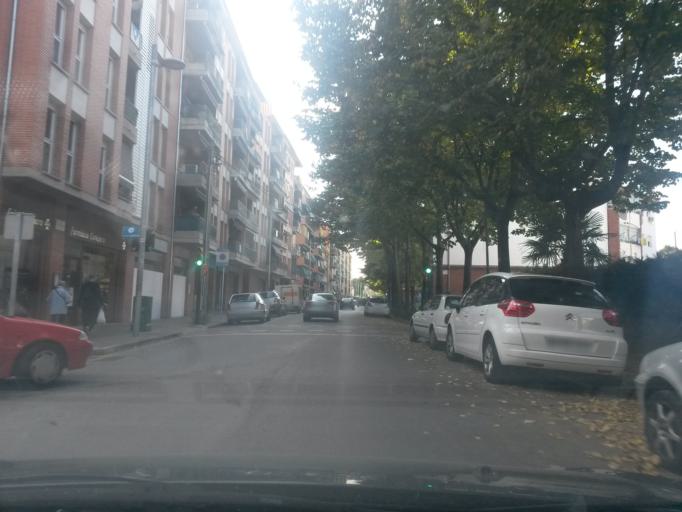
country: ES
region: Catalonia
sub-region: Provincia de Girona
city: Girona
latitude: 41.9749
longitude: 2.8133
